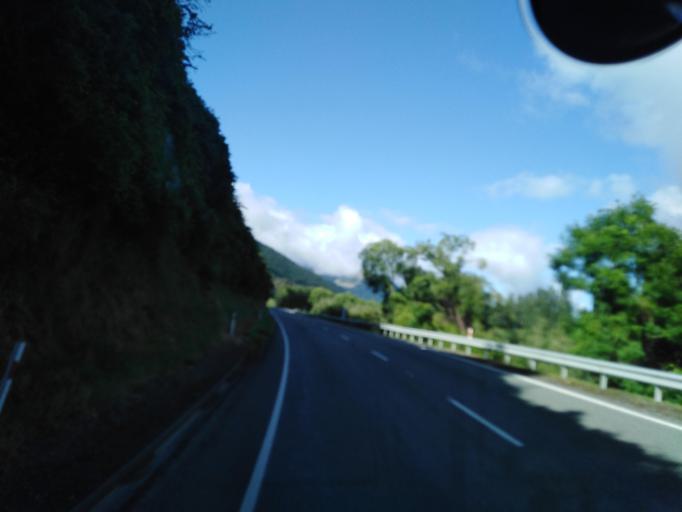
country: NZ
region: Nelson
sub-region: Nelson City
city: Nelson
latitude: -41.2830
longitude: 173.6425
